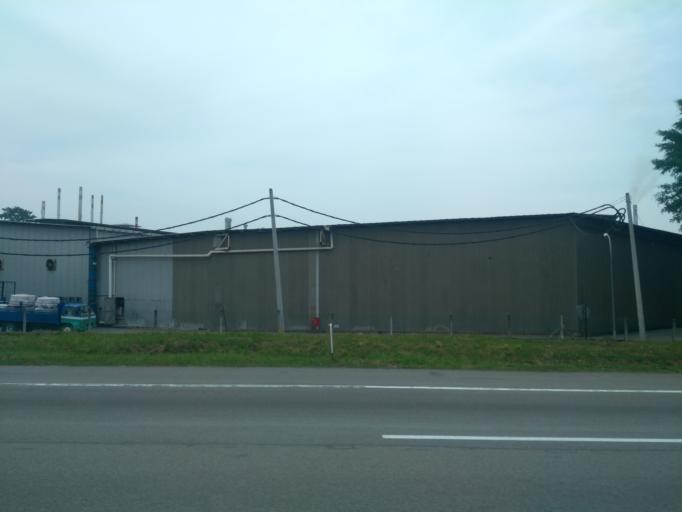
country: MY
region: Perak
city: Parit Buntar
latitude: 5.1544
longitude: 100.5105
